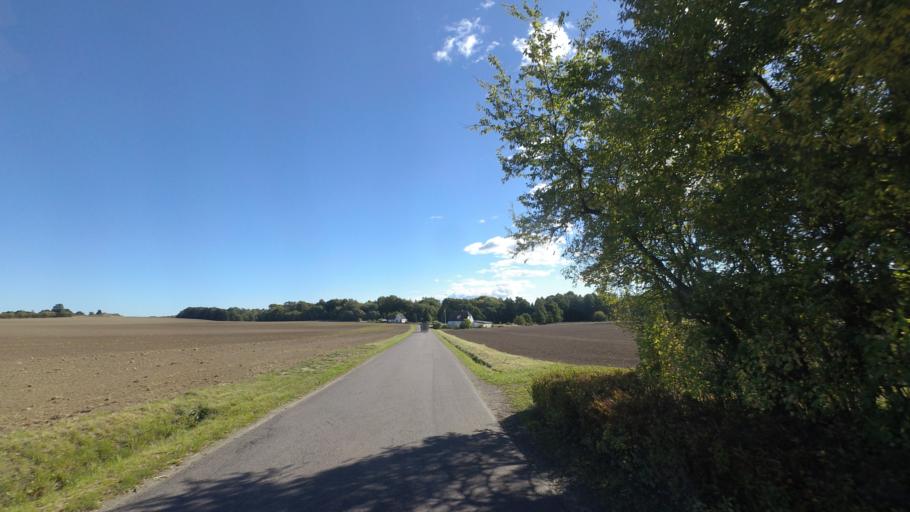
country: DK
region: Capital Region
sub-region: Bornholm Kommune
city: Akirkeby
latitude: 55.1350
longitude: 15.0192
